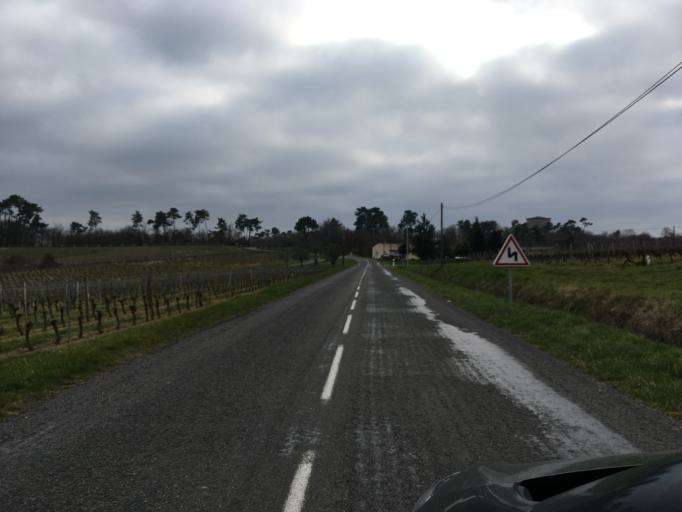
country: FR
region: Aquitaine
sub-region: Departement de la Gironde
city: Saint-Ciers-sur-Gironde
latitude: 45.3231
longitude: -0.5944
